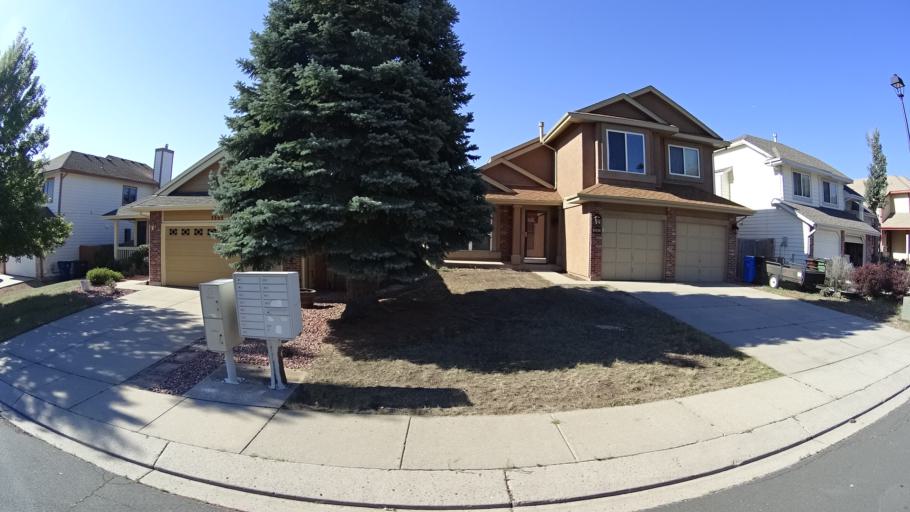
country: US
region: Colorado
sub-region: El Paso County
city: Black Forest
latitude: 38.9574
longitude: -104.7582
